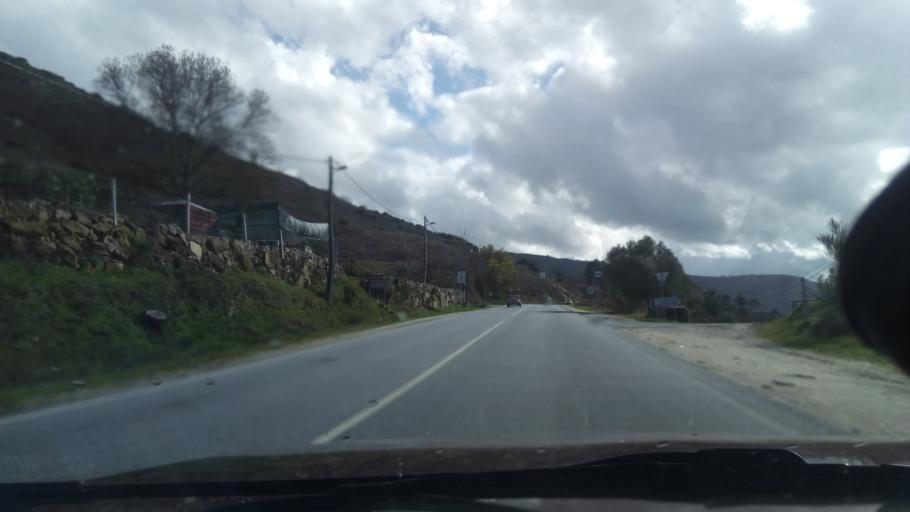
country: PT
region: Guarda
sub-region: Guarda
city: Guarda
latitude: 40.5790
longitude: -7.2950
